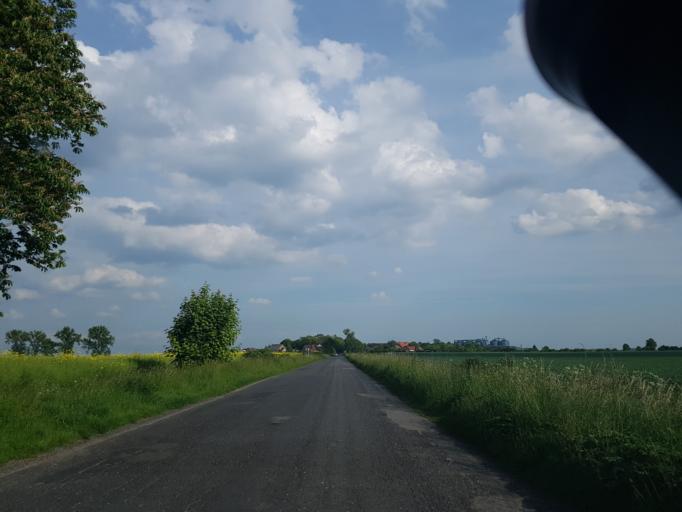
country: PL
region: Lower Silesian Voivodeship
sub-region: Powiat strzelinski
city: Wiazow
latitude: 50.8595
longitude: 17.1784
